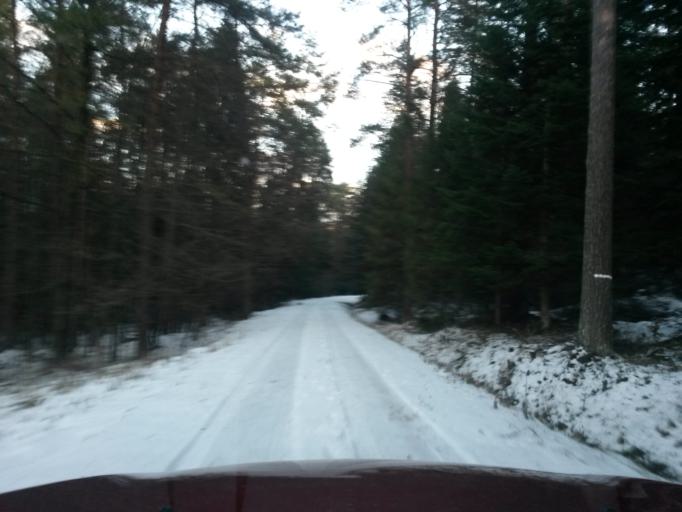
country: SK
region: Kosicky
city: Medzev
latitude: 48.7855
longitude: 20.8020
